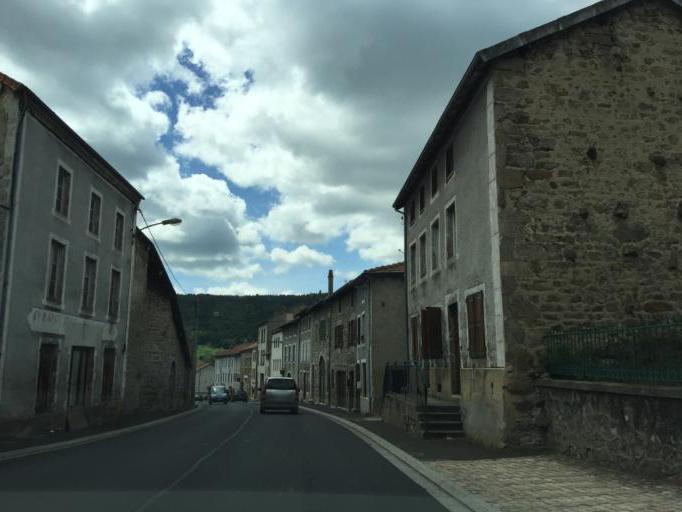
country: FR
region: Rhone-Alpes
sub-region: Departement de la Loire
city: Usson-en-Forez
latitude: 45.5295
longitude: 3.9188
